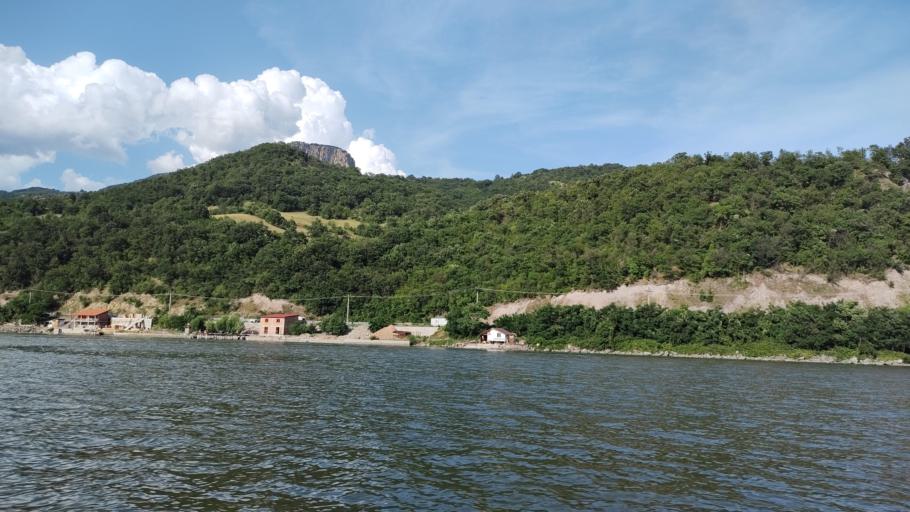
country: RO
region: Mehedinti
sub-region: Comuna Svinita
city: Svinita
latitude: 44.5521
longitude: 22.0345
